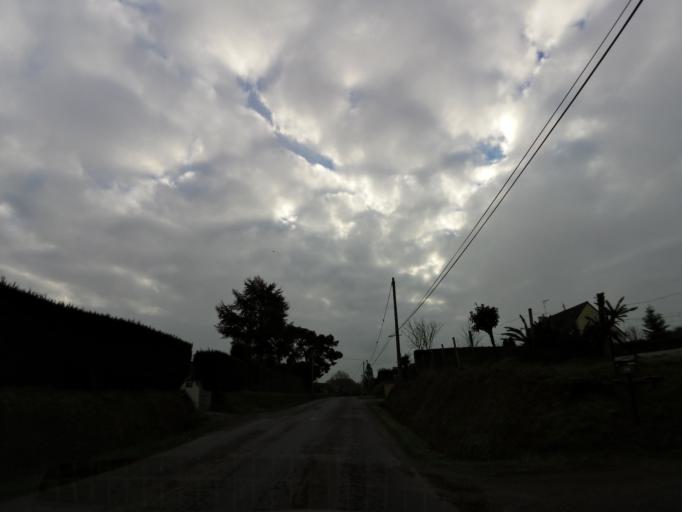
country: FR
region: Brittany
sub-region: Departement d'Ille-et-Vilaine
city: Chanteloup
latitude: 47.9714
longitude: -1.6476
